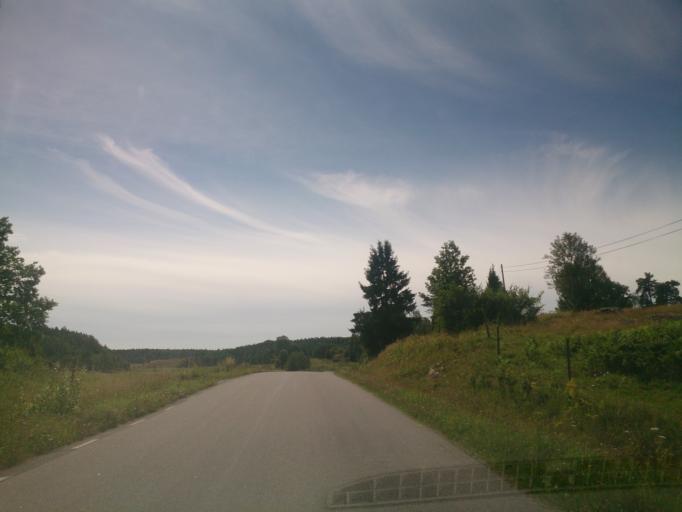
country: SE
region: OEstergoetland
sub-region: Valdemarsviks Kommun
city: Valdemarsvik
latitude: 58.2934
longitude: 16.6690
